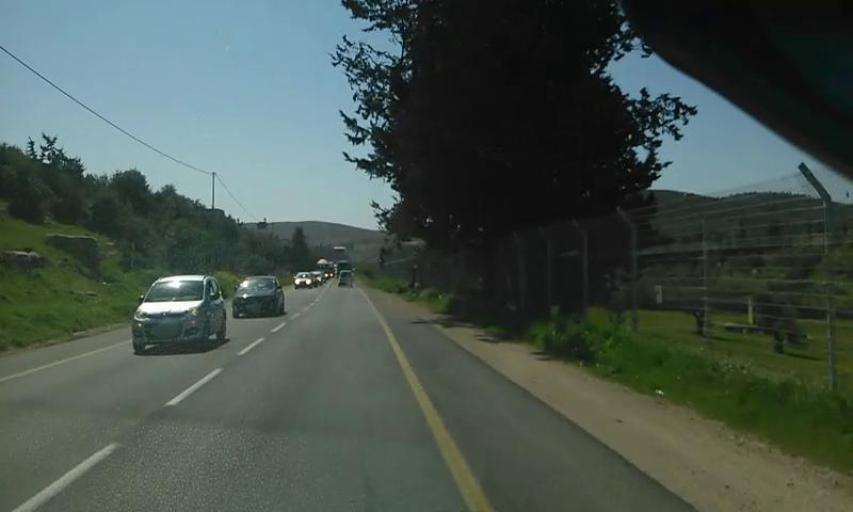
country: PS
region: West Bank
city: Shuyukh al `Arrub
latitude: 31.6297
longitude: 35.1323
